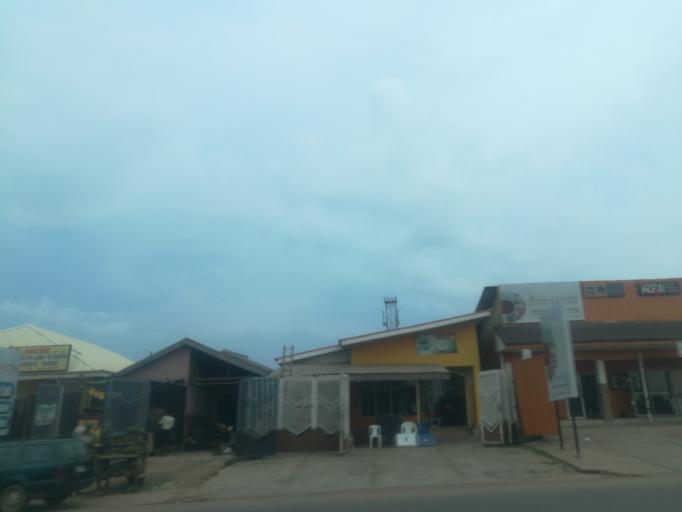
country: NG
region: Oyo
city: Ibadan
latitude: 7.4369
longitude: 3.9097
